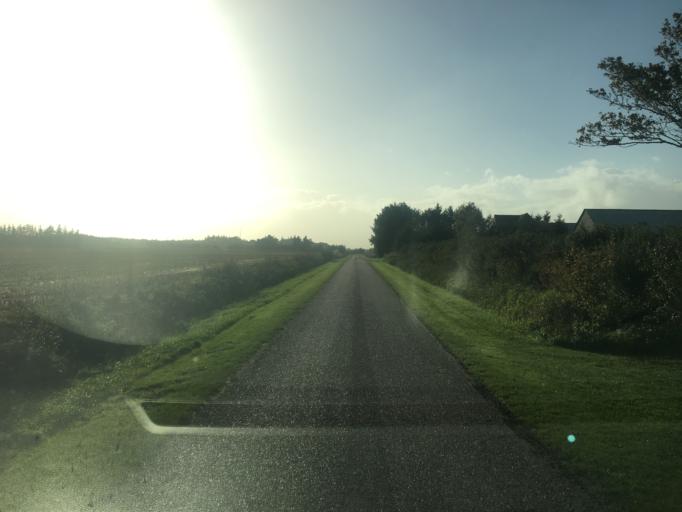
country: DK
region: South Denmark
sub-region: Tonder Kommune
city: Tonder
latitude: 54.9741
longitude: 8.8475
